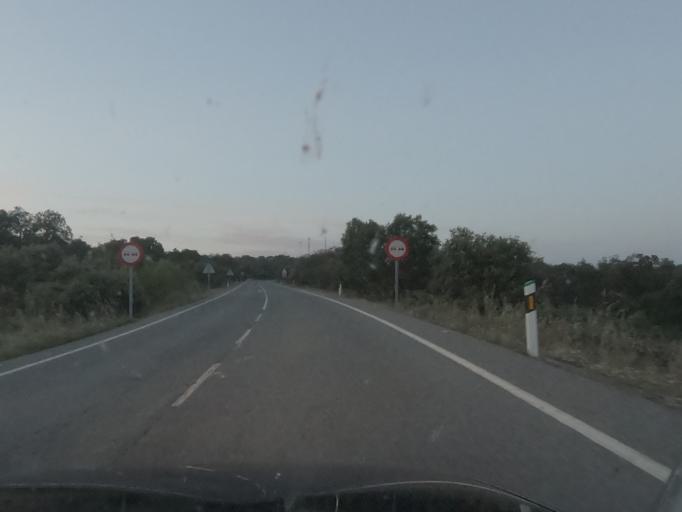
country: ES
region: Extremadura
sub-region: Provincia de Caceres
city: Alcantara
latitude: 39.7391
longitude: -6.9029
